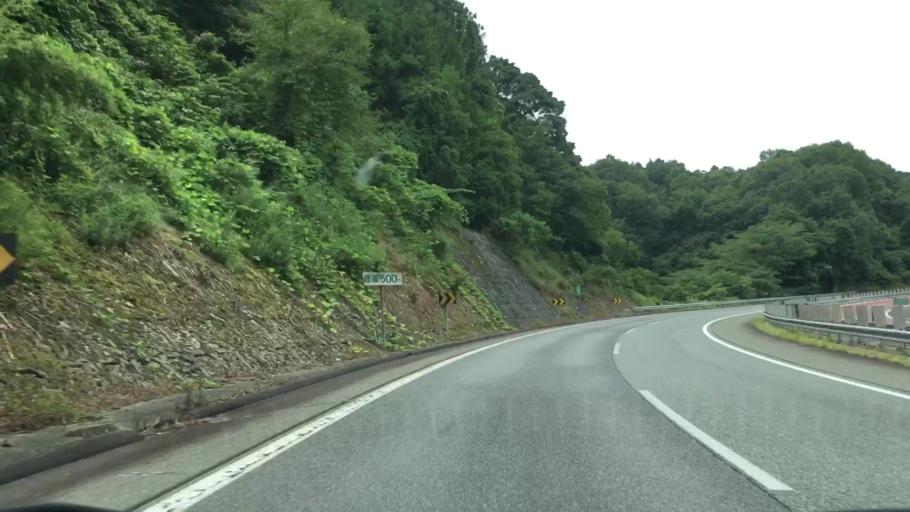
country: JP
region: Hiroshima
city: Shobara
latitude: 34.8910
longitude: 133.2247
